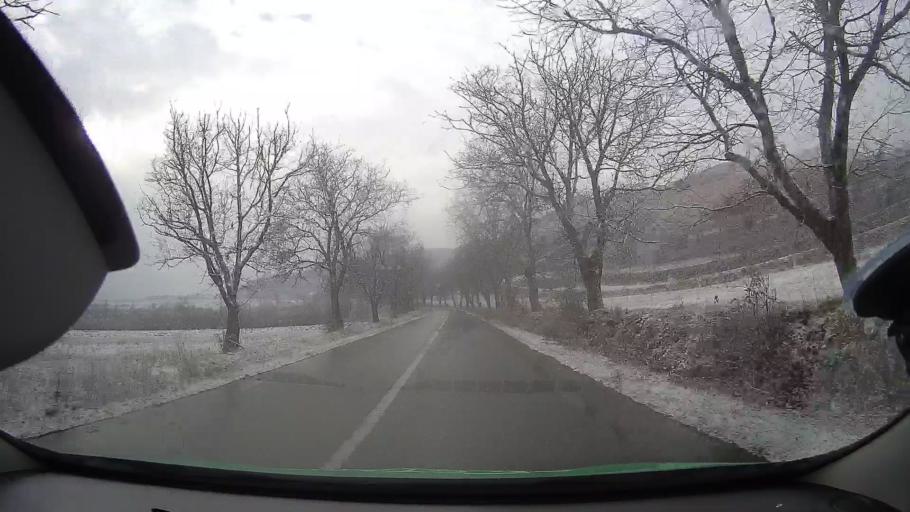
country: RO
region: Alba
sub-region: Comuna Rimetea
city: Rimetea
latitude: 46.4395
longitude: 23.5632
